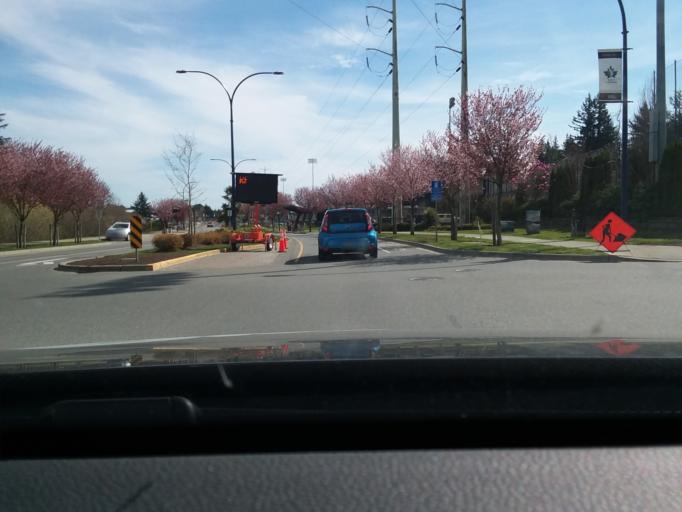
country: CA
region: British Columbia
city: Langford
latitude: 48.4439
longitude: -123.5281
